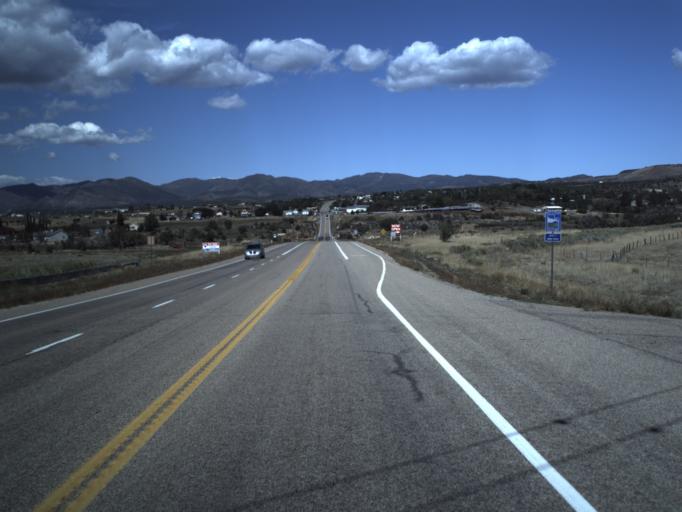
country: US
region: Utah
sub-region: Washington County
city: Ivins
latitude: 37.3270
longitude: -113.6932
